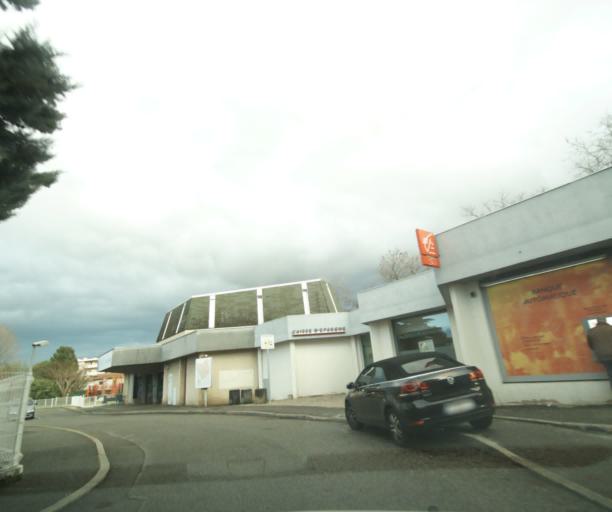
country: FR
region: Rhone-Alpes
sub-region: Departement de la Drome
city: Bourg-les-Valence
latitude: 44.9501
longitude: 4.8993
